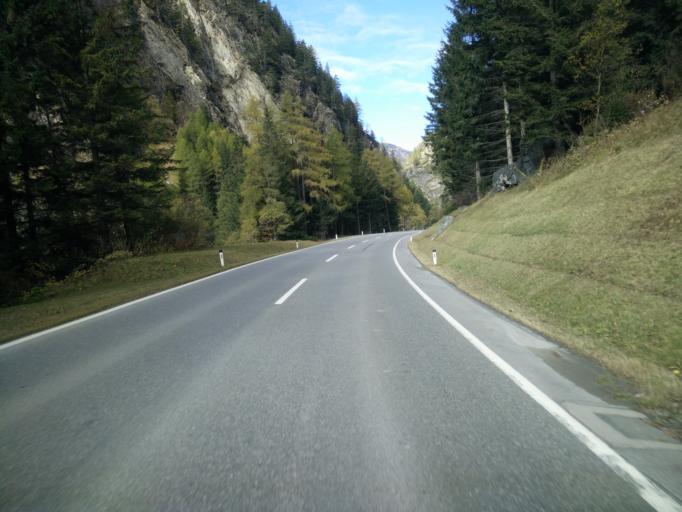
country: AT
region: Tyrol
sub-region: Politischer Bezirk Imst
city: Soelden
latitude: 47.0351
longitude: 10.9869
